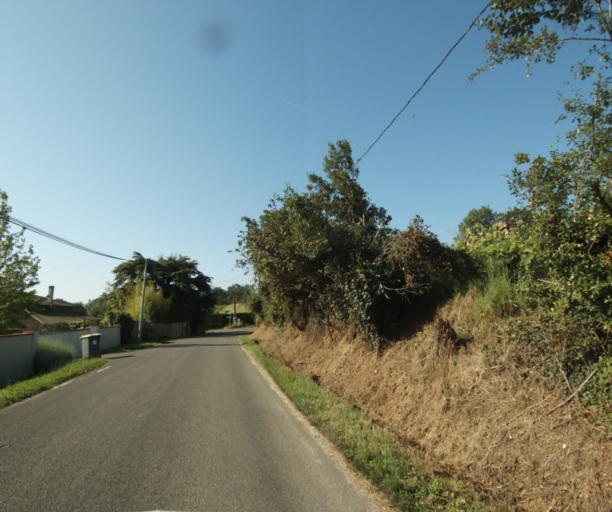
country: FR
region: Midi-Pyrenees
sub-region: Departement du Tarn-et-Garonne
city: Saint-Nauphary
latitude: 44.0146
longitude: 1.4311
